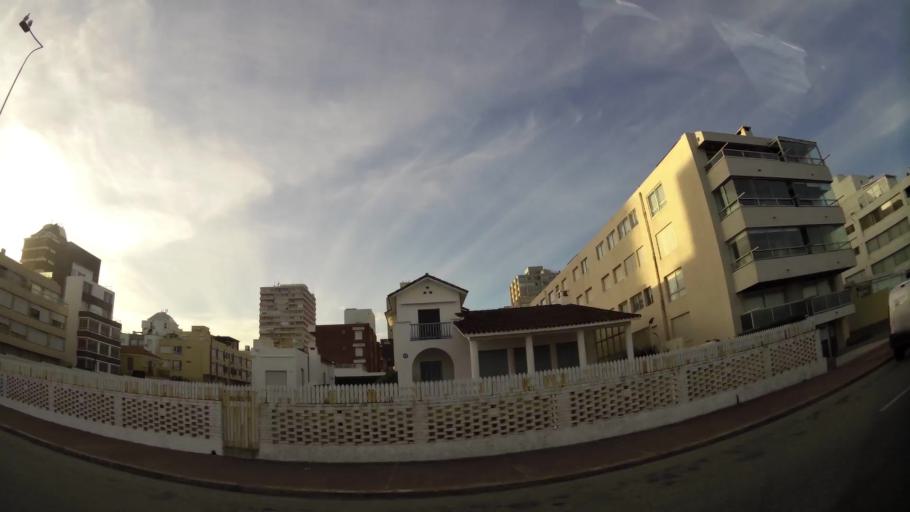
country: UY
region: Maldonado
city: Punta del Este
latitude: -34.9620
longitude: -54.9399
